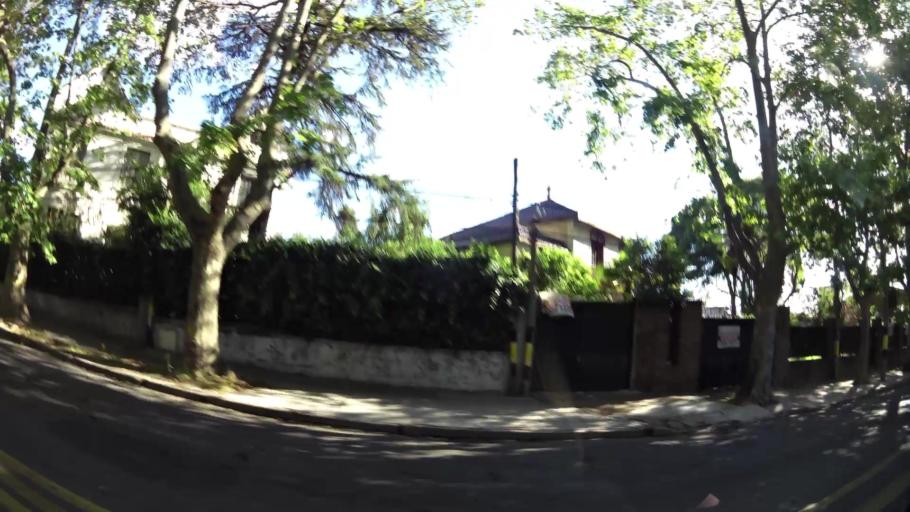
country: UY
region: Montevideo
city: Montevideo
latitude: -34.8579
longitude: -56.1945
